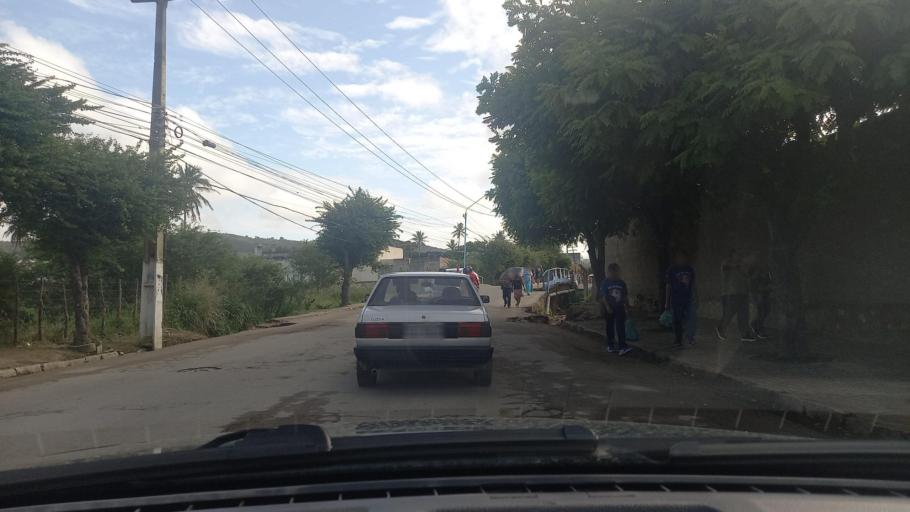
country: BR
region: Pernambuco
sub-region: Vitoria De Santo Antao
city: Vitoria de Santo Antao
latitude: -8.1044
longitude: -35.2835
